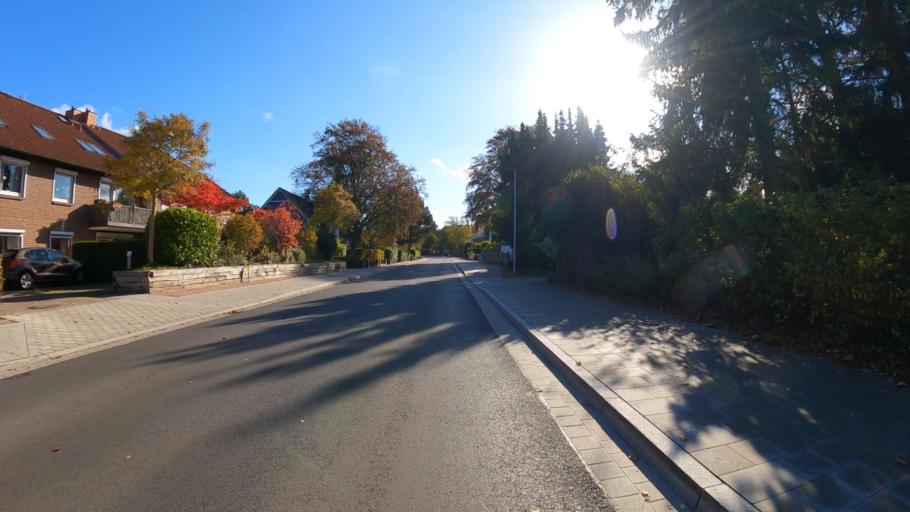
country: DE
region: Schleswig-Holstein
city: Ahrensburg
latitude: 53.6851
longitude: 10.2290
